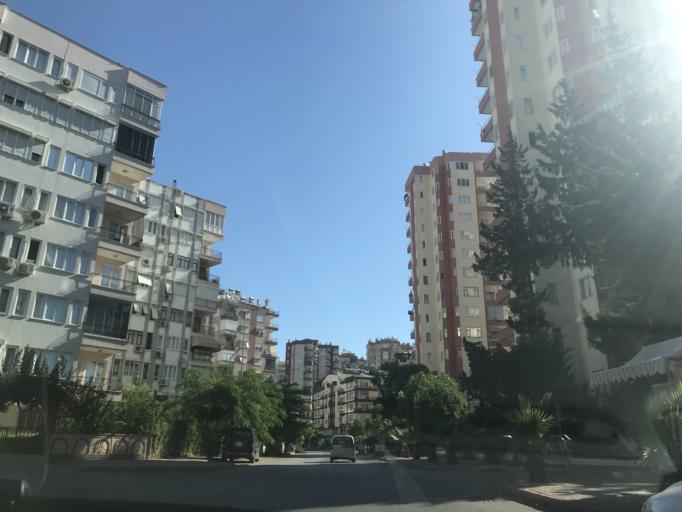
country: TR
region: Antalya
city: Antalya
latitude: 36.8952
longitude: 30.6295
